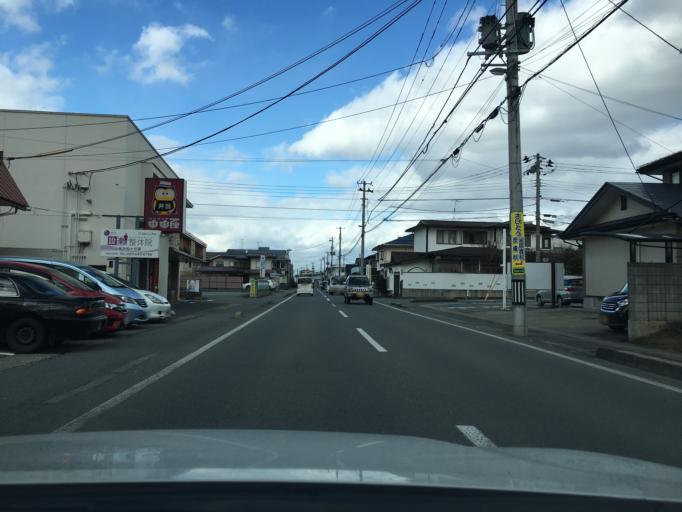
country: JP
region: Yamagata
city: Yamagata-shi
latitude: 38.2455
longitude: 140.3126
